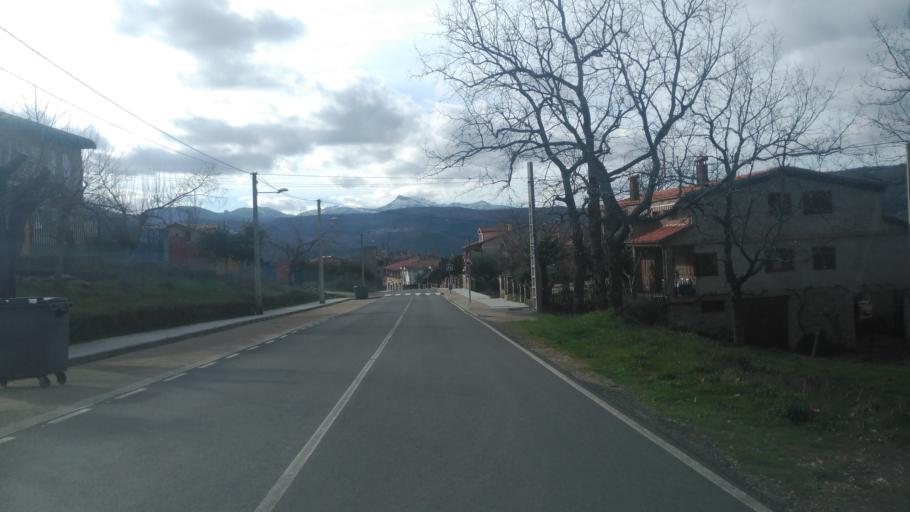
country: ES
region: Castille and Leon
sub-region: Provincia de Salamanca
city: Miranda del Castanar
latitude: 40.4835
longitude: -5.9919
